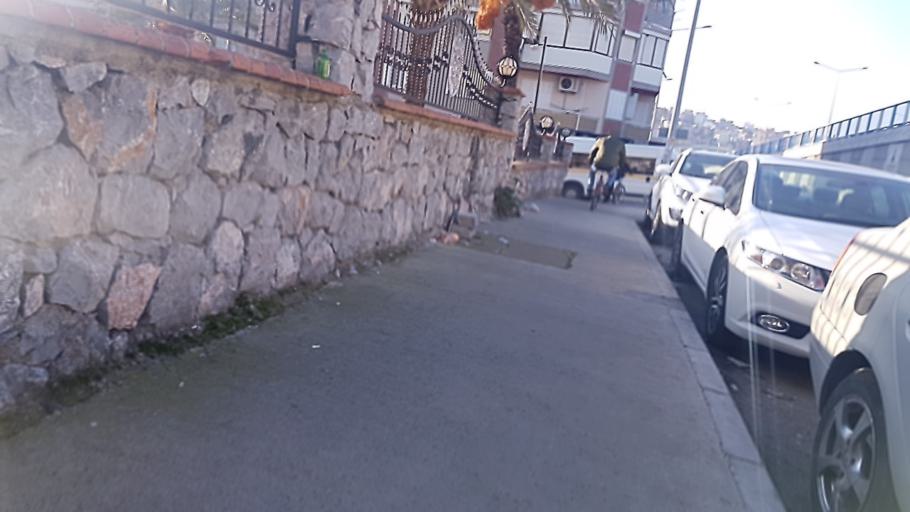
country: TR
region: Izmir
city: Izmir
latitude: 38.4009
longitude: 27.1492
